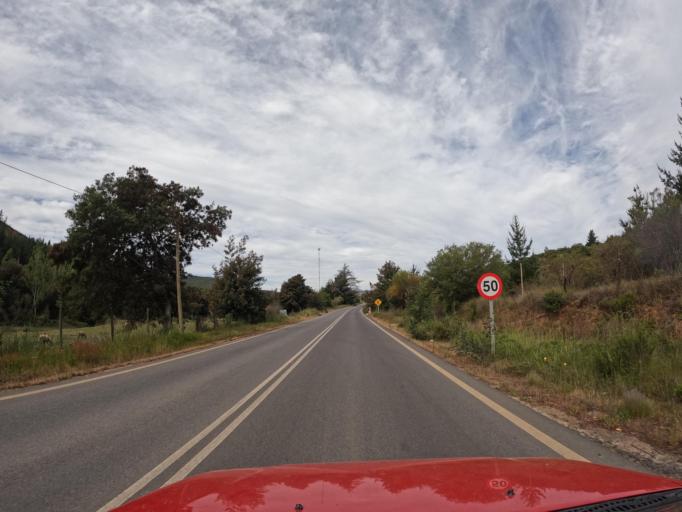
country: CL
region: Maule
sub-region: Provincia de Talca
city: Talca
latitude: -35.3230
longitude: -71.9380
